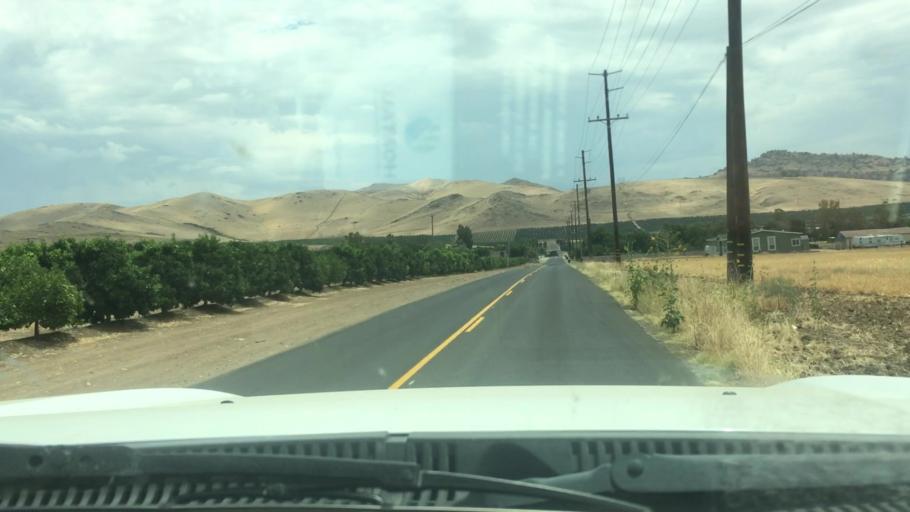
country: US
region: California
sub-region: Tulare County
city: Porterville
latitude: 36.0964
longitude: -119.0240
